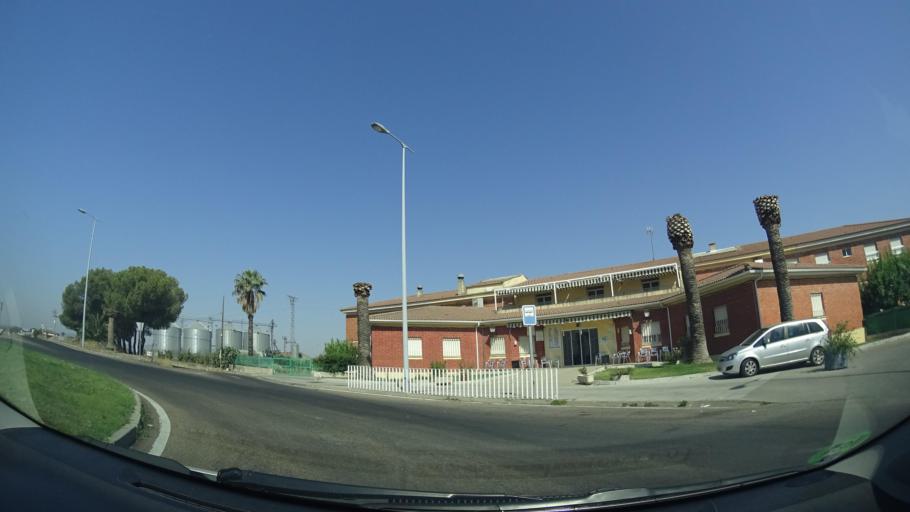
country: ES
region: Extremadura
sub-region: Provincia de Caceres
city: Miajadas
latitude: 39.1437
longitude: -5.9251
